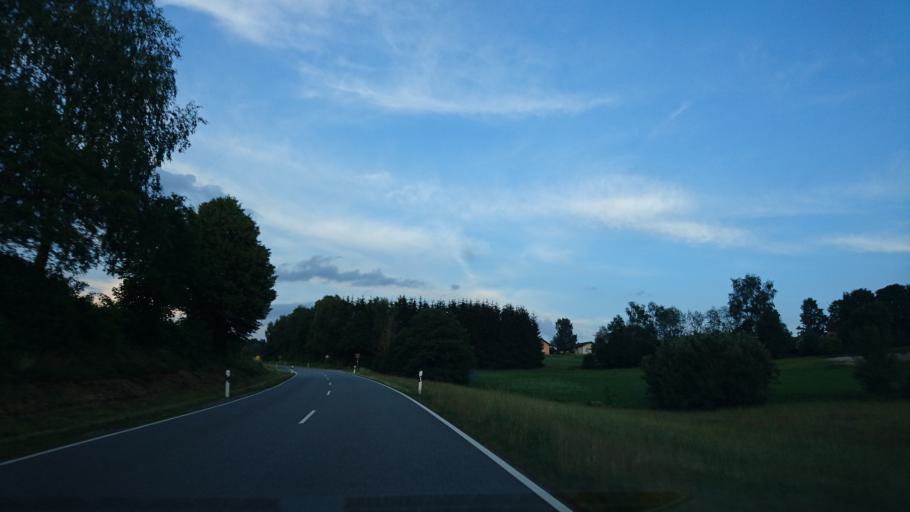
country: DE
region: Bavaria
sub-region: Lower Bavaria
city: Grafenau
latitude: 48.8743
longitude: 13.4142
